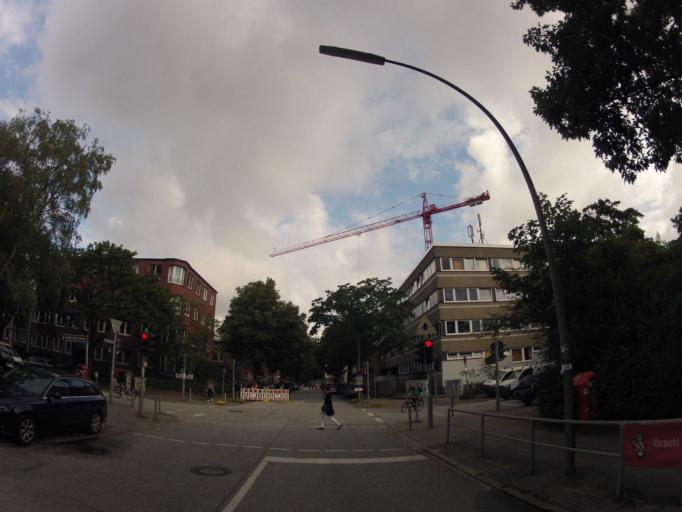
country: DE
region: Hamburg
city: Hamburg
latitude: 53.5736
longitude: 10.0259
